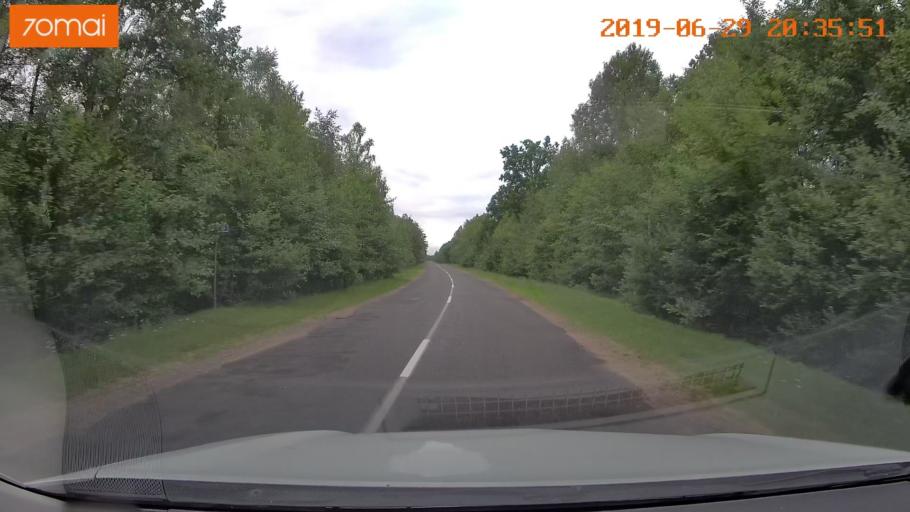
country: BY
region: Brest
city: Hantsavichy
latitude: 52.5199
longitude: 26.3539
